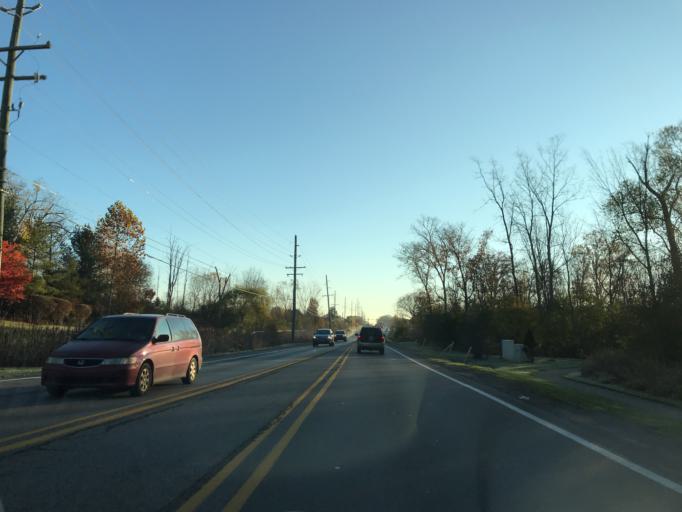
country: US
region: Michigan
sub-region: Oakland County
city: Novi
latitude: 42.4664
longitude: -83.4818
